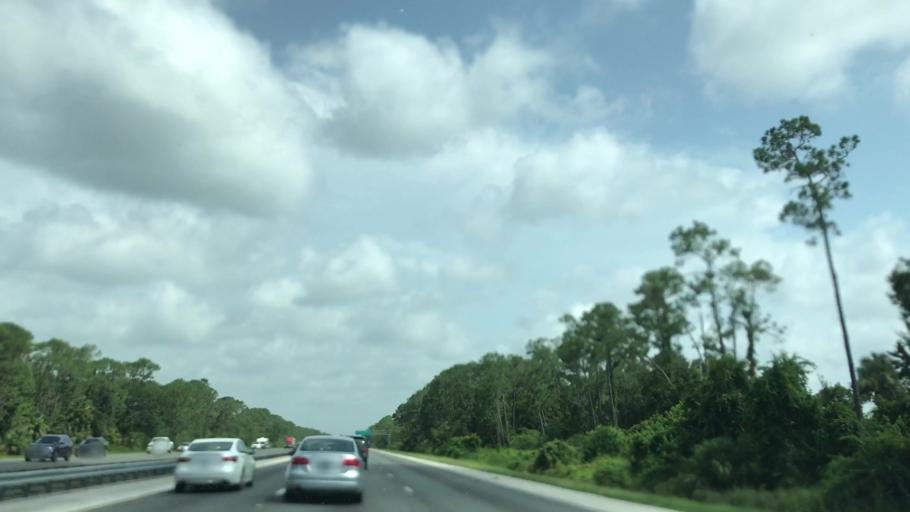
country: US
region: Florida
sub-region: Volusia County
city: Ormond-by-the-Sea
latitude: 29.3805
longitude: -81.1450
